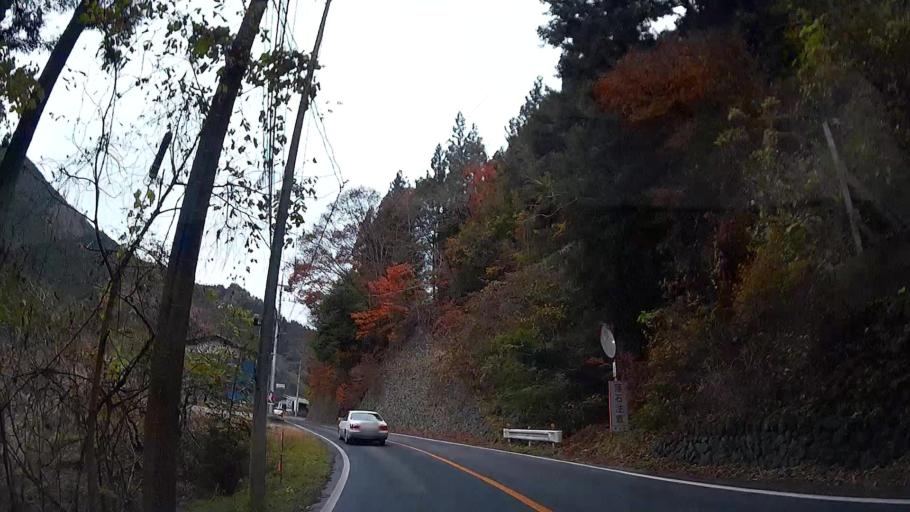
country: JP
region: Saitama
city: Chichibu
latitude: 35.9414
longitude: 138.9461
